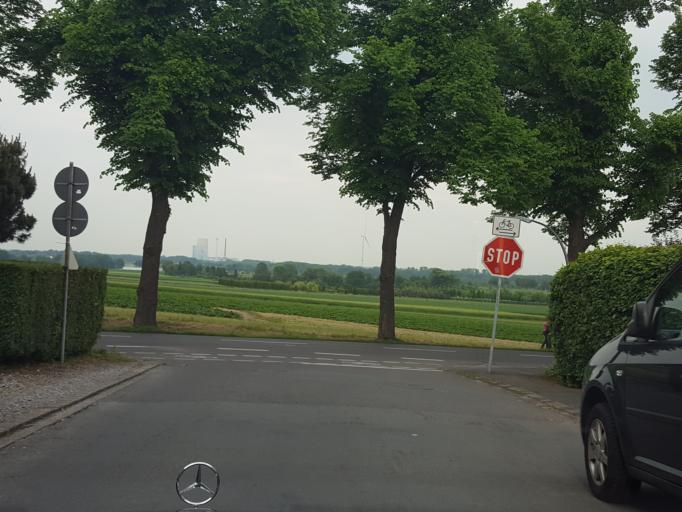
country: DE
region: North Rhine-Westphalia
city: Oer-Erkenschwick
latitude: 51.6159
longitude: 7.2565
